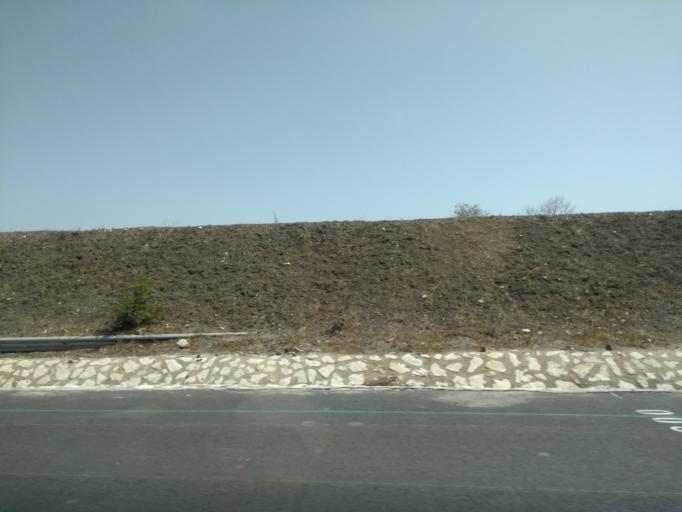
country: SN
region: Thies
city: Pout
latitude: 14.7351
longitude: -17.1749
